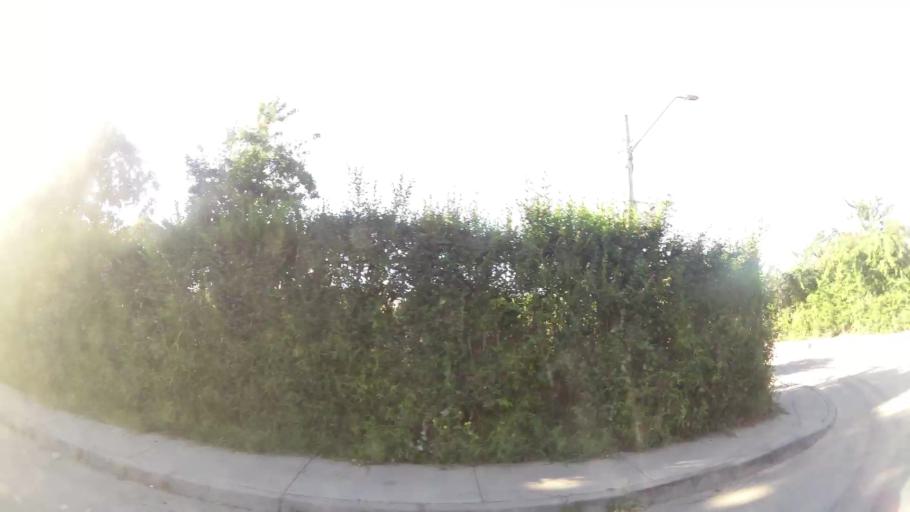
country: CL
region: Santiago Metropolitan
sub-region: Provincia de Maipo
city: San Bernardo
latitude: -33.6422
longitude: -70.7078
